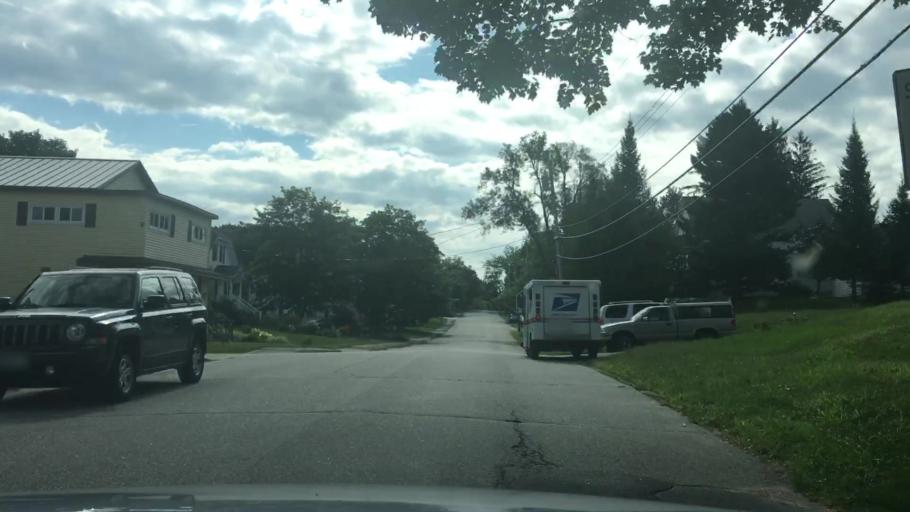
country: US
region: Maine
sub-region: Androscoggin County
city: Lewiston
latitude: 44.1120
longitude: -70.2056
